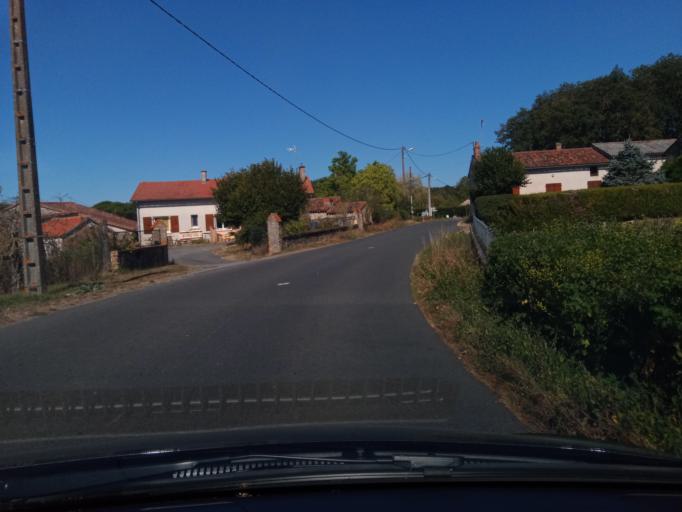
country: FR
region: Poitou-Charentes
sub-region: Departement de la Vienne
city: Montmorillon
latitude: 46.4791
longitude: 0.8951
